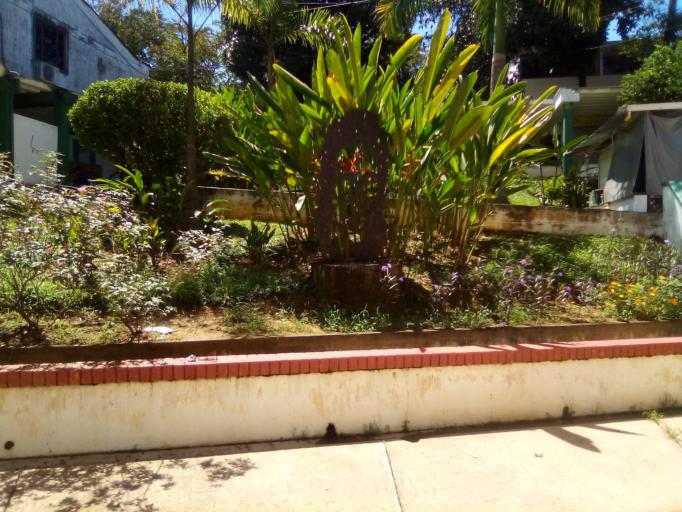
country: CO
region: Caqueta
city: Florencia
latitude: 1.6206
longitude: -75.6046
